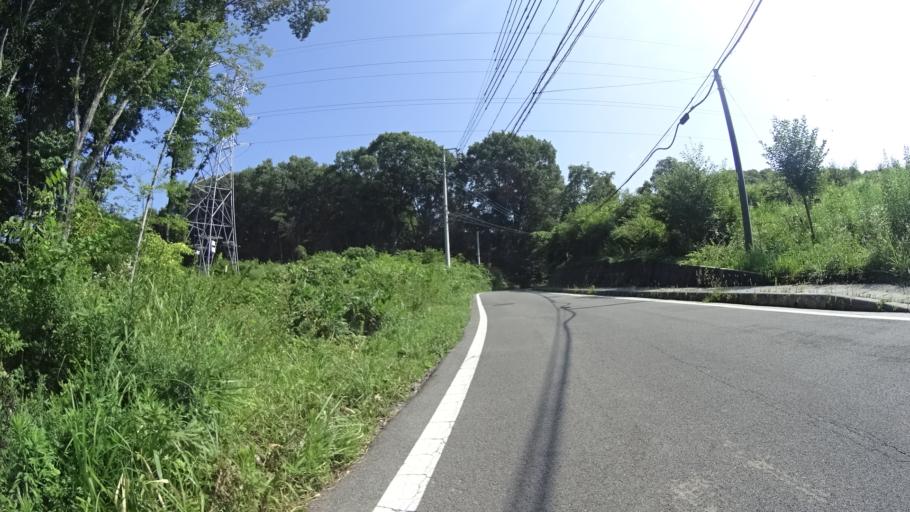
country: JP
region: Yamanashi
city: Nirasaki
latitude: 35.8664
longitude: 138.3286
